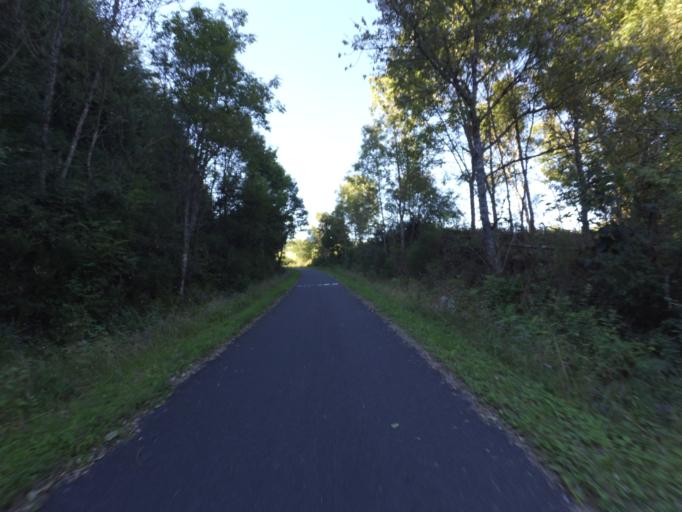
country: DE
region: Rheinland-Pfalz
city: Mehren
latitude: 50.1767
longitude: 6.8710
